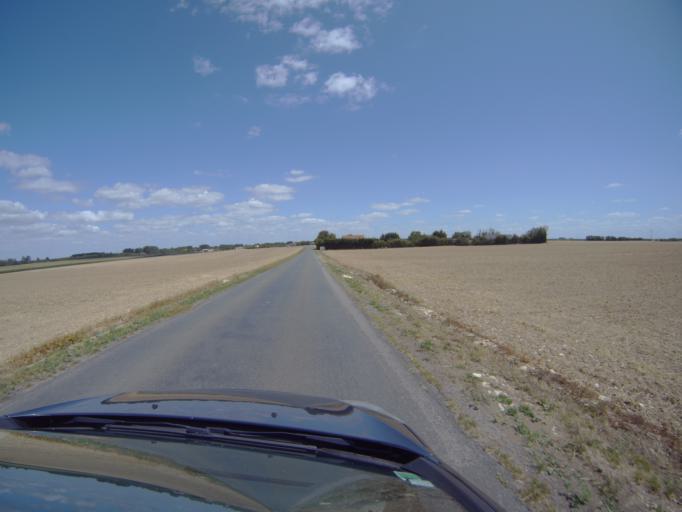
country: FR
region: Poitou-Charentes
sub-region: Departement de la Charente-Maritime
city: Courcon
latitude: 46.2478
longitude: -0.7798
